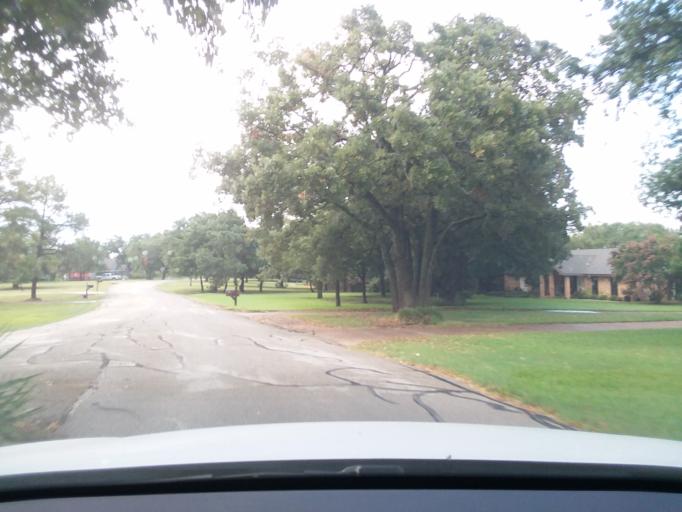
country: US
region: Texas
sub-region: Denton County
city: Double Oak
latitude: 33.0685
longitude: -97.1088
